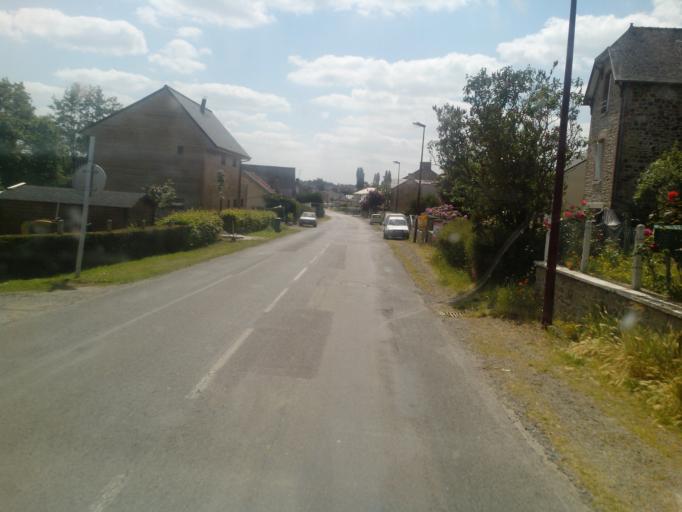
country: FR
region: Brittany
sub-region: Departement d'Ille-et-Vilaine
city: Montreuil-sur-Ille
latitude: 48.3107
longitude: -1.6653
